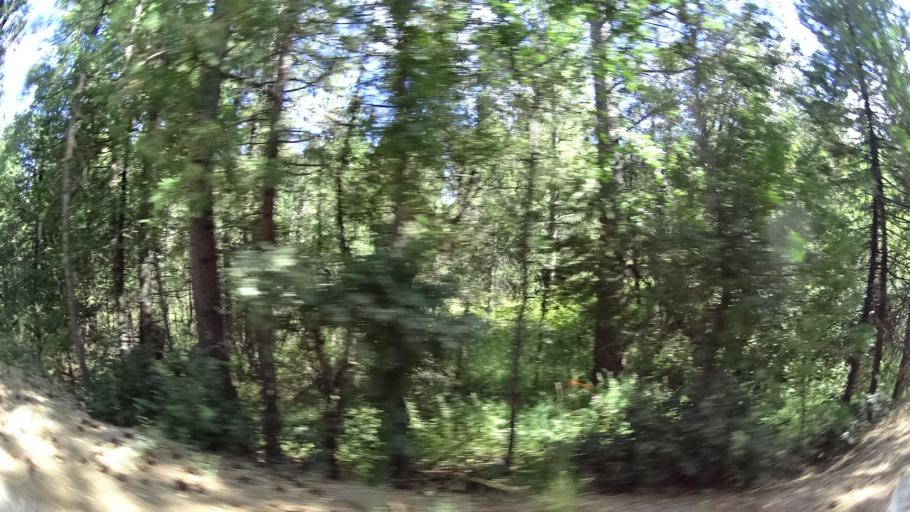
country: US
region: California
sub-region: Amador County
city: Pioneer
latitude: 38.3747
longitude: -120.4570
